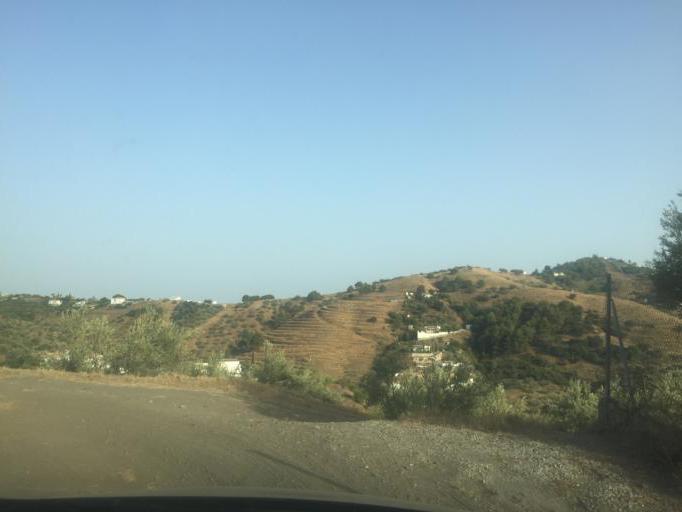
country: ES
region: Andalusia
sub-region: Provincia de Malaga
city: Competa
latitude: 36.8077
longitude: -3.9362
